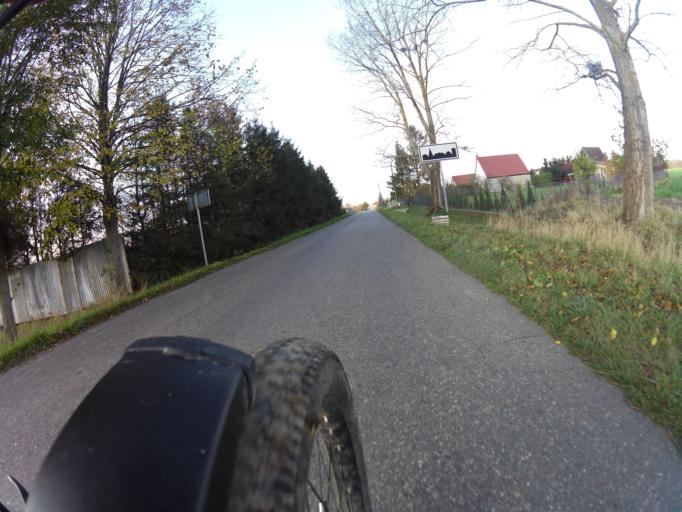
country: PL
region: Pomeranian Voivodeship
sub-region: Powiat pucki
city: Krokowa
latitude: 54.7572
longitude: 18.1840
